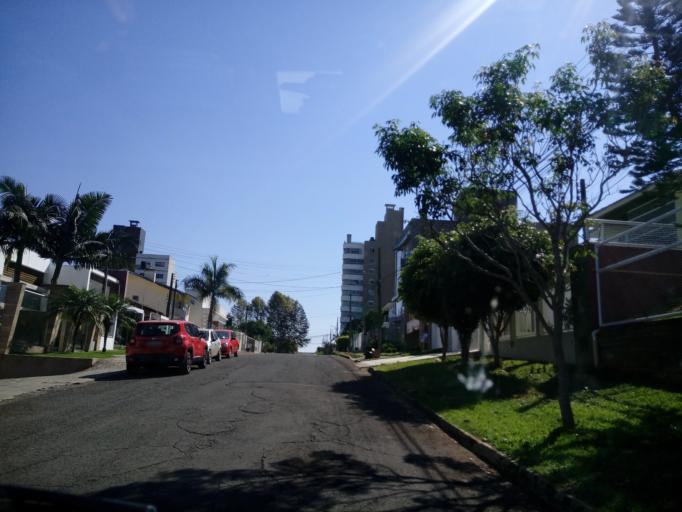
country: BR
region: Santa Catarina
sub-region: Chapeco
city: Chapeco
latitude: -27.0927
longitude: -52.5995
